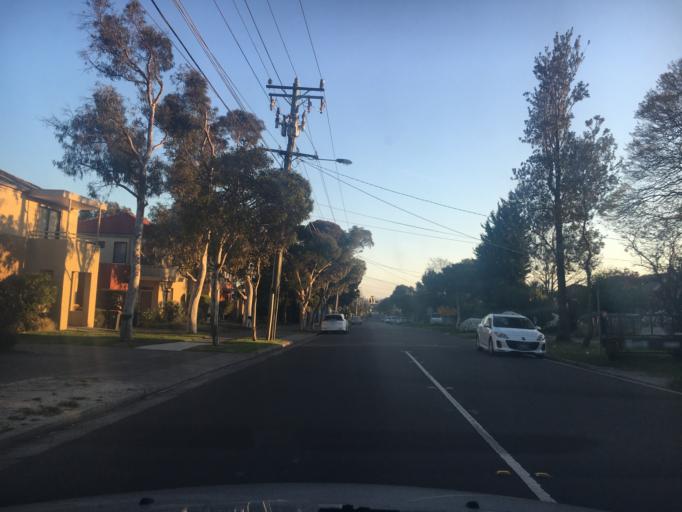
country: AU
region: Victoria
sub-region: Monash
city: Clayton
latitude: -37.9227
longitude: 145.1271
